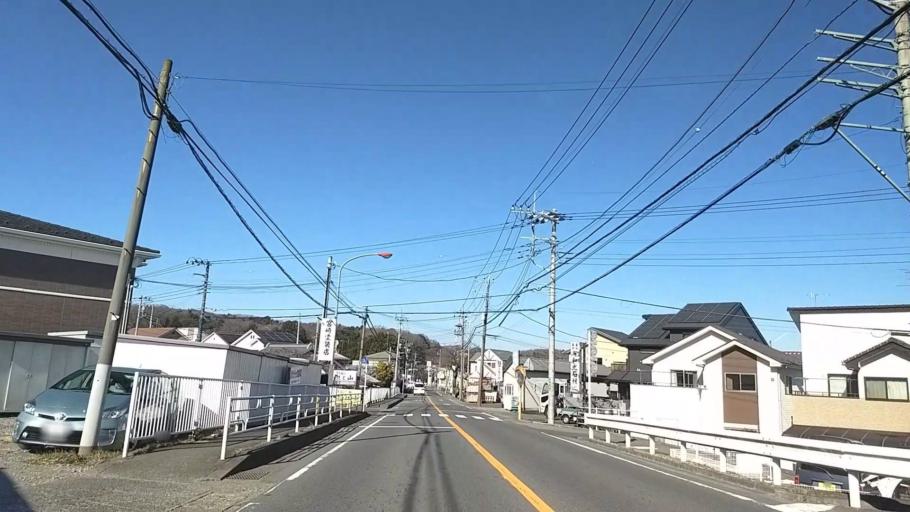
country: JP
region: Tokyo
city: Hachioji
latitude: 35.6017
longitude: 139.3017
